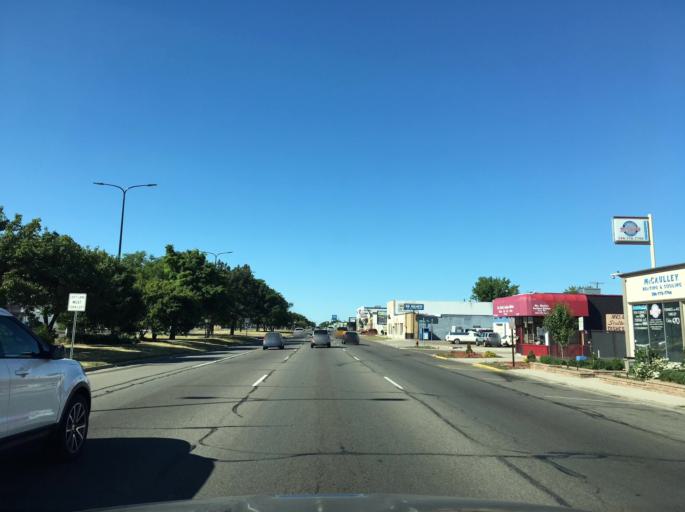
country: US
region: Michigan
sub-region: Macomb County
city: Eastpointe
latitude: 42.4540
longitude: -82.9648
